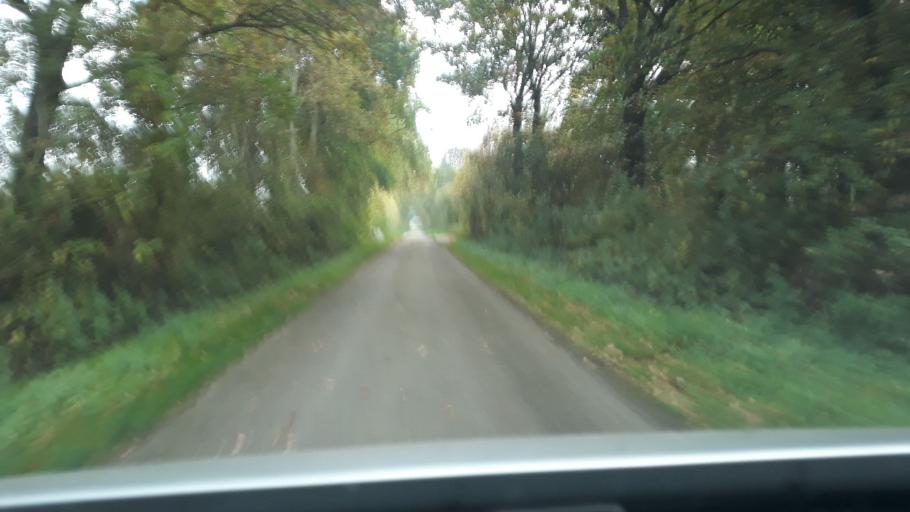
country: DE
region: Schleswig-Holstein
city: Klein Bennebek
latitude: 54.4053
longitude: 9.4715
